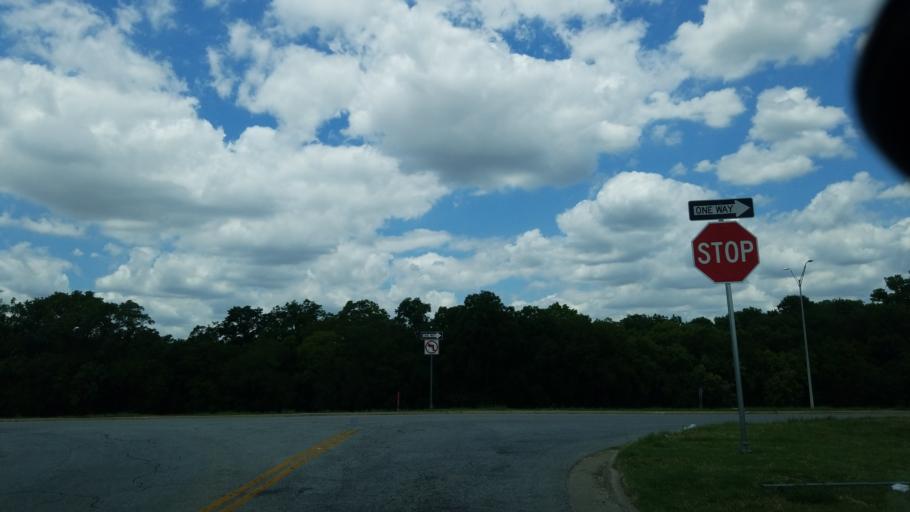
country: US
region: Texas
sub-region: Dallas County
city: Dallas
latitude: 32.7466
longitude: -96.7456
